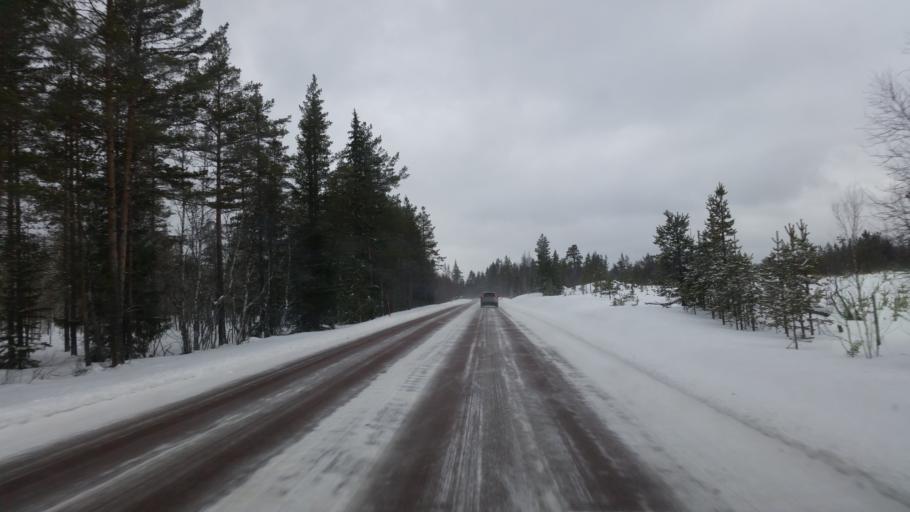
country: SE
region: Jaemtland
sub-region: Bergs Kommun
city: Hoverberg
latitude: 62.4114
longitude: 14.6202
